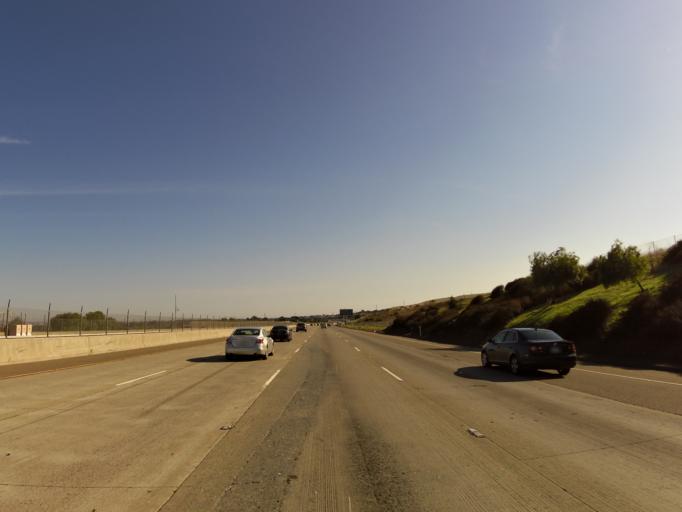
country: US
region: California
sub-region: Contra Costa County
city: Bay Point
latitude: 38.0217
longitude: -121.9605
